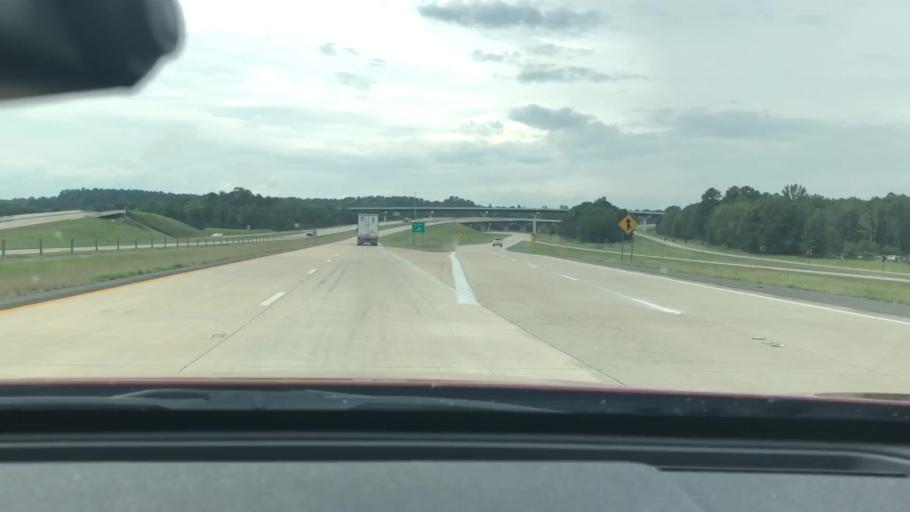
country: US
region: Texas
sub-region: Bowie County
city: Texarkana
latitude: 33.3916
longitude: -94.0154
